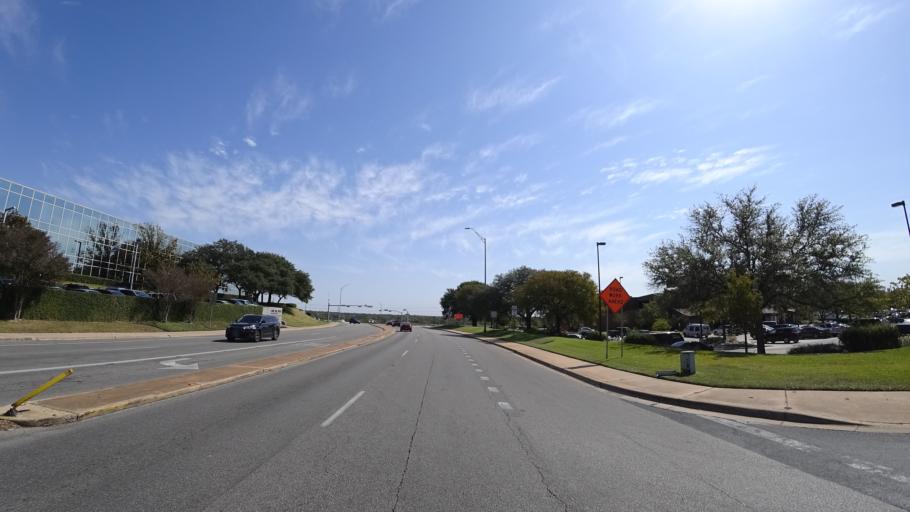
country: US
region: Texas
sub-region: Travis County
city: West Lake Hills
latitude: 30.3524
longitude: -97.7510
